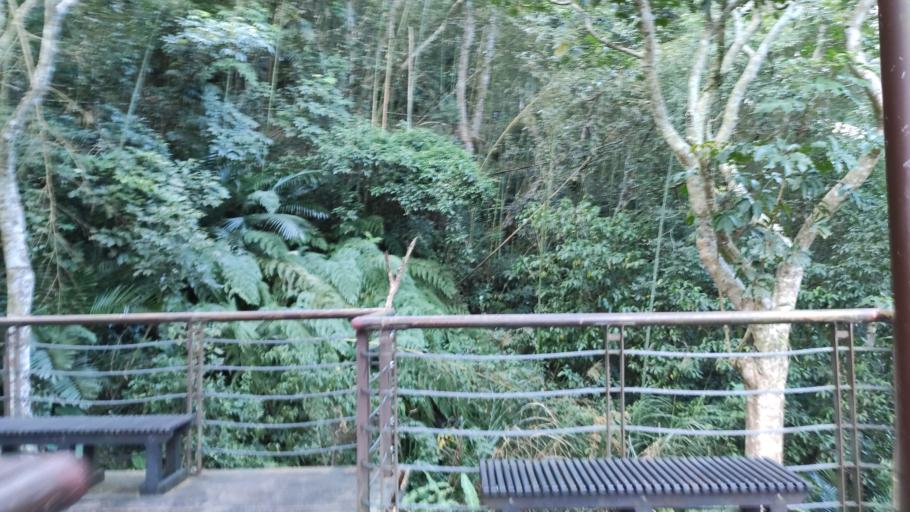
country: TW
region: Taiwan
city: Daxi
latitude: 24.7896
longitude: 121.3740
